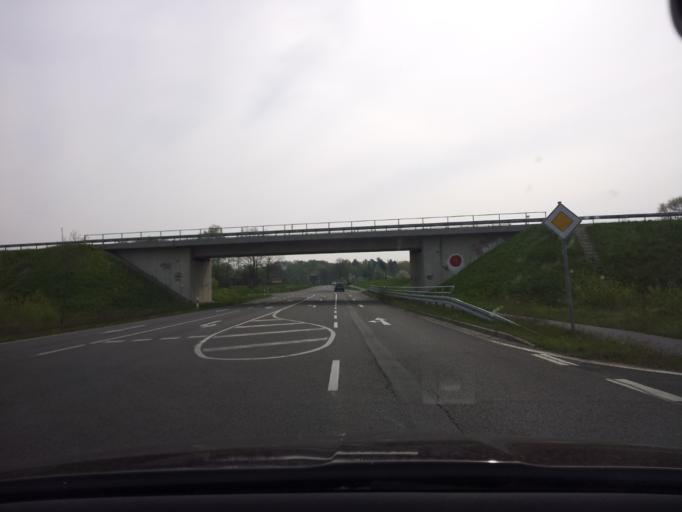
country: DE
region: Brandenburg
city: Luckau
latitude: 51.8535
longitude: 13.6854
